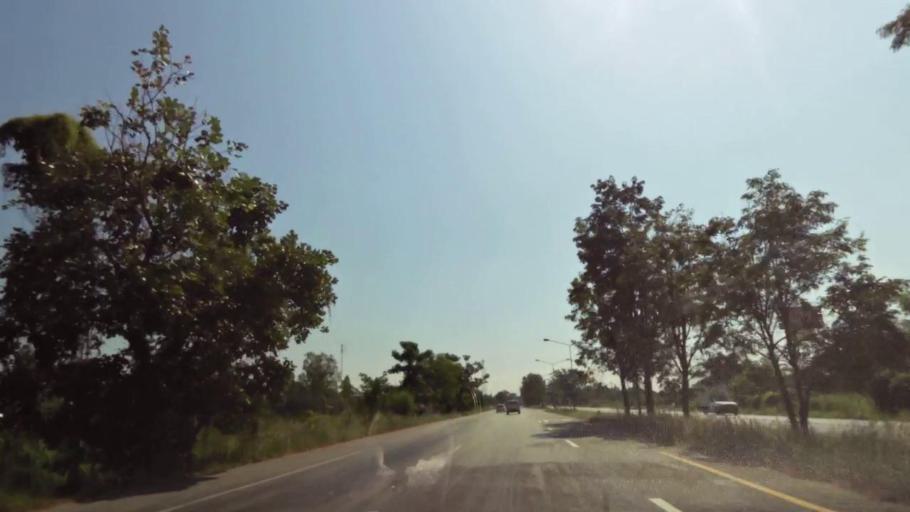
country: TH
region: Nakhon Sawan
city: Kao Liao
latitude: 15.8768
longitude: 100.1161
